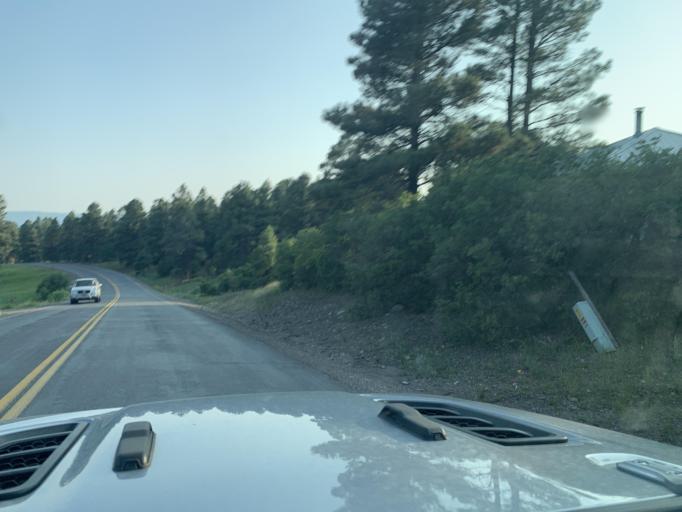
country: US
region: Colorado
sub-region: Archuleta County
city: Pagosa Springs
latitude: 37.2755
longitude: -107.0973
